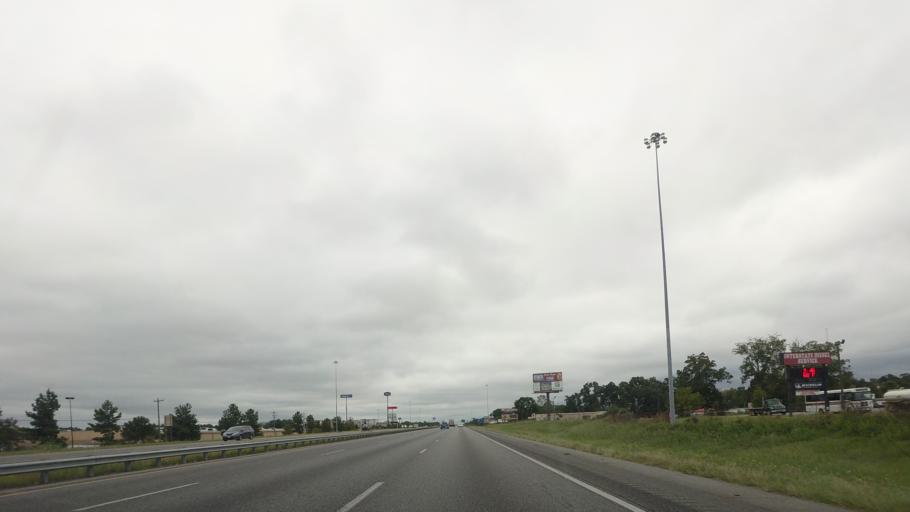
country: US
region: Georgia
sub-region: Lowndes County
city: Remerton
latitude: 30.8271
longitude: -83.3219
